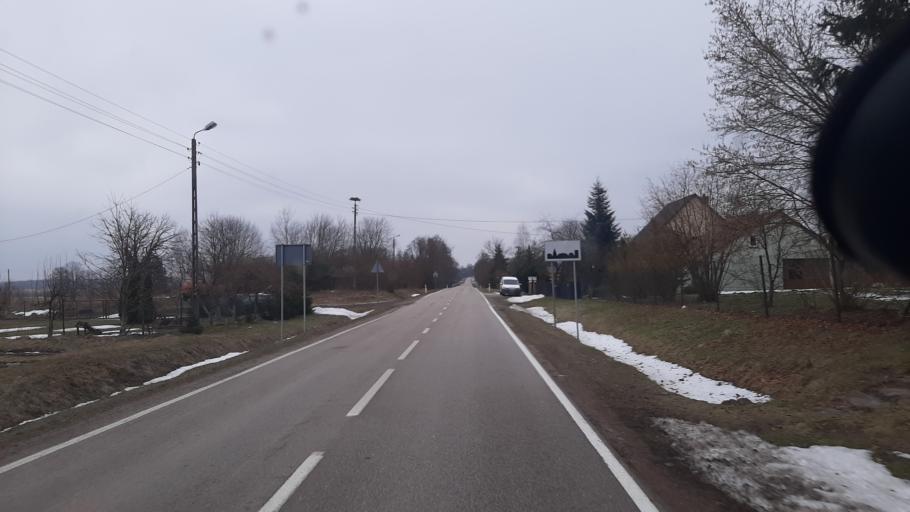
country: PL
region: Lublin Voivodeship
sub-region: Powiat wlodawski
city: Wlodawa
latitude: 51.4835
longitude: 23.6269
